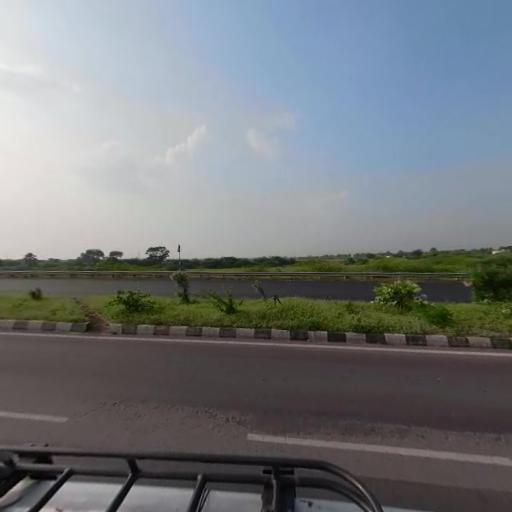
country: IN
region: Telangana
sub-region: Nalgonda
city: Suriapet
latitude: 17.1626
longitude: 79.5214
